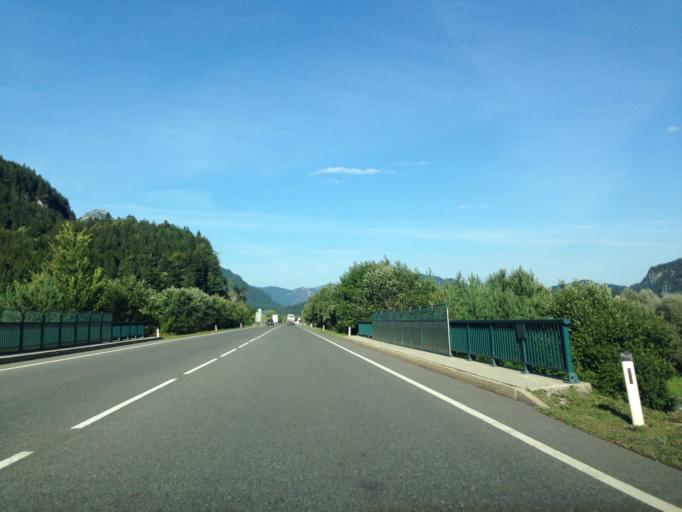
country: AT
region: Tyrol
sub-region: Politischer Bezirk Reutte
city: Pflach
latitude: 47.5248
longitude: 10.7030
